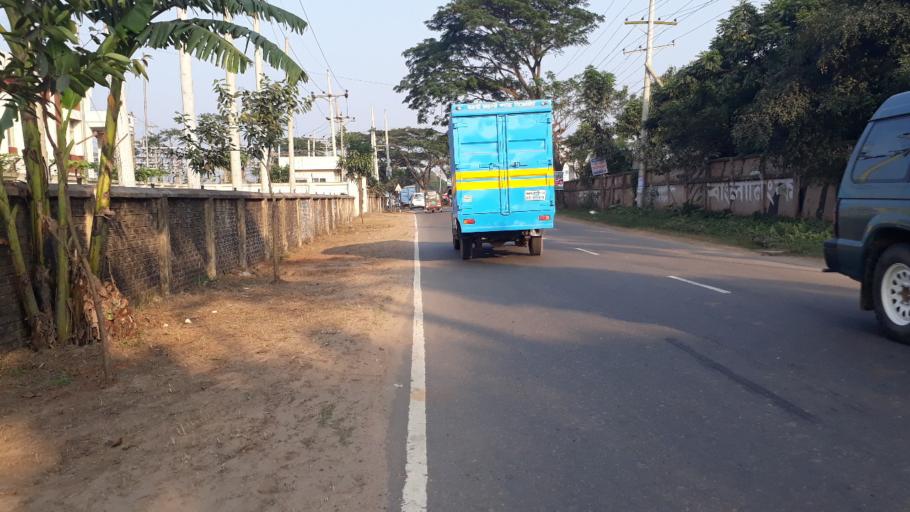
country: BD
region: Dhaka
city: Tungi
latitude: 23.8738
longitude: 90.2804
